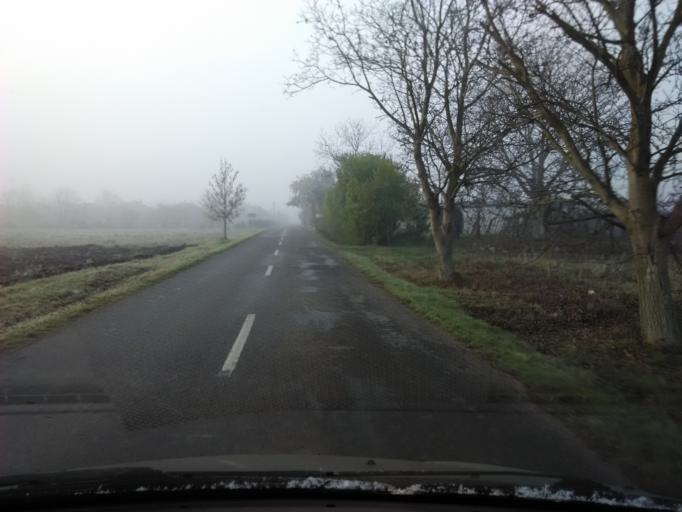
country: SK
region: Nitriansky
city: Tlmace
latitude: 48.2519
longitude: 18.5322
